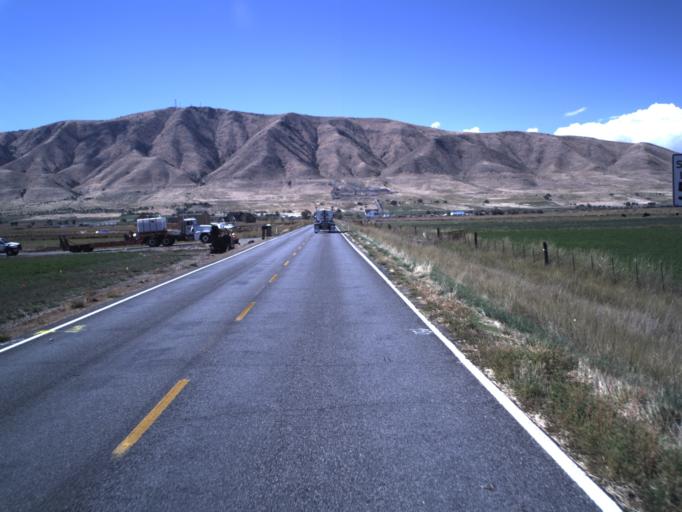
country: US
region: Utah
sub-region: Utah County
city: Benjamin
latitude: 40.0979
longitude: -111.7552
